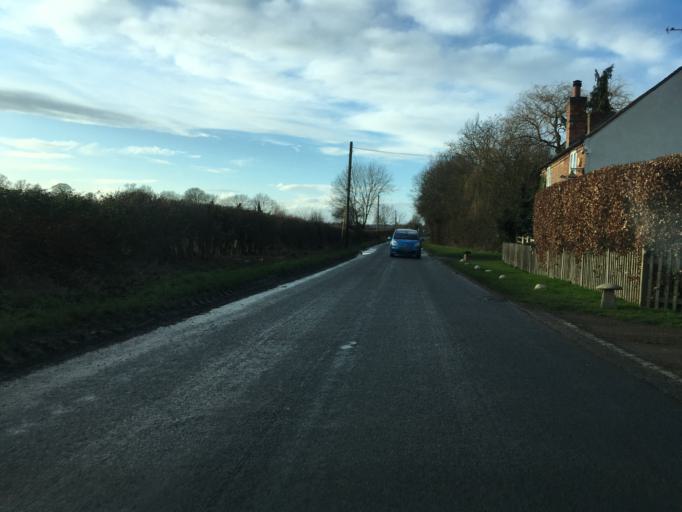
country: GB
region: England
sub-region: Warwickshire
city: Alcester
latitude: 52.2239
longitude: -1.8075
